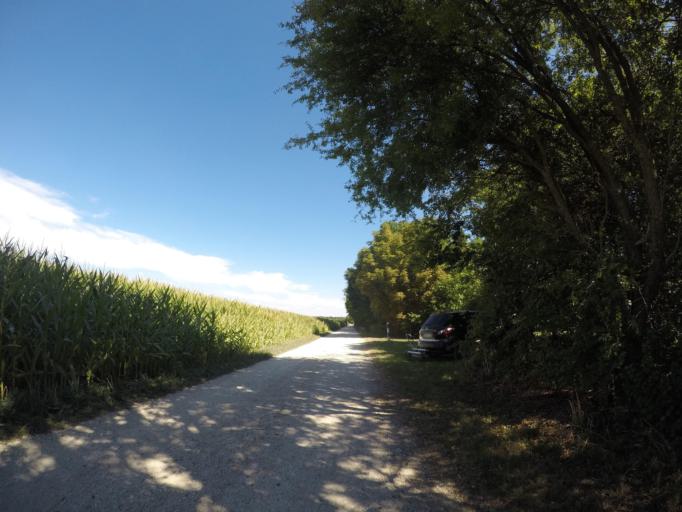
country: DE
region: Bavaria
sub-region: Swabia
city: Senden
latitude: 48.3627
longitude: 10.0569
